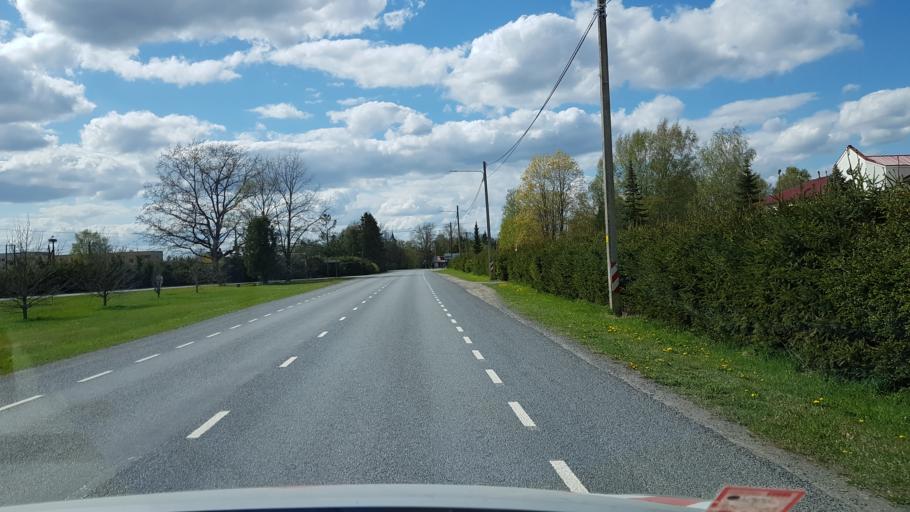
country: EE
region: Polvamaa
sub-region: Polva linn
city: Polva
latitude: 58.2822
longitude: 27.0528
